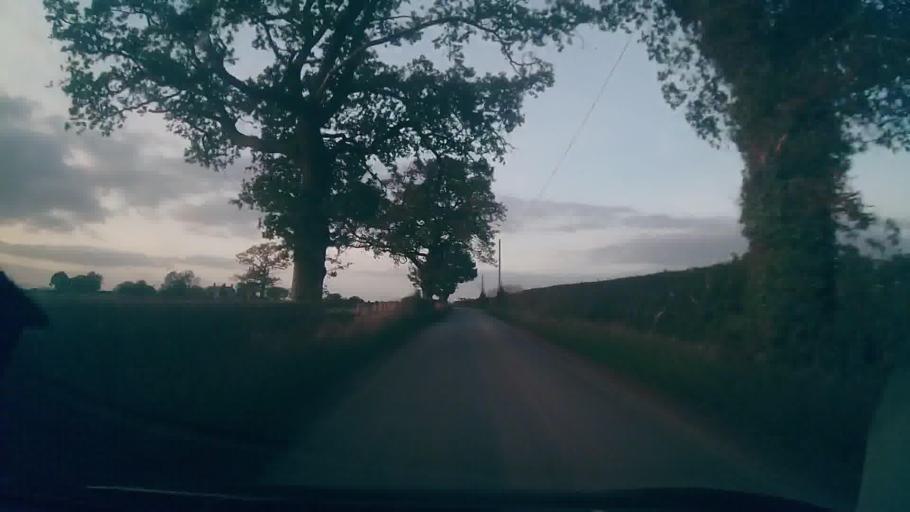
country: GB
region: England
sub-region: Shropshire
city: Clive
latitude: 52.8243
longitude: -2.7263
